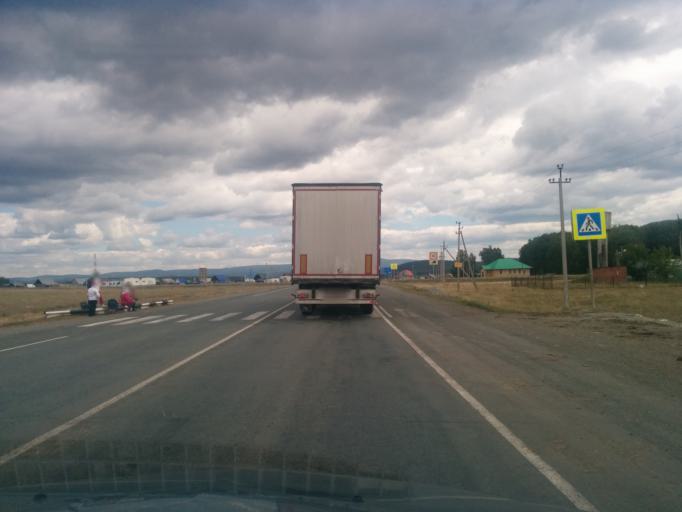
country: RU
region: Bashkortostan
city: Lomovka
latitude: 53.8812
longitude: 58.1055
